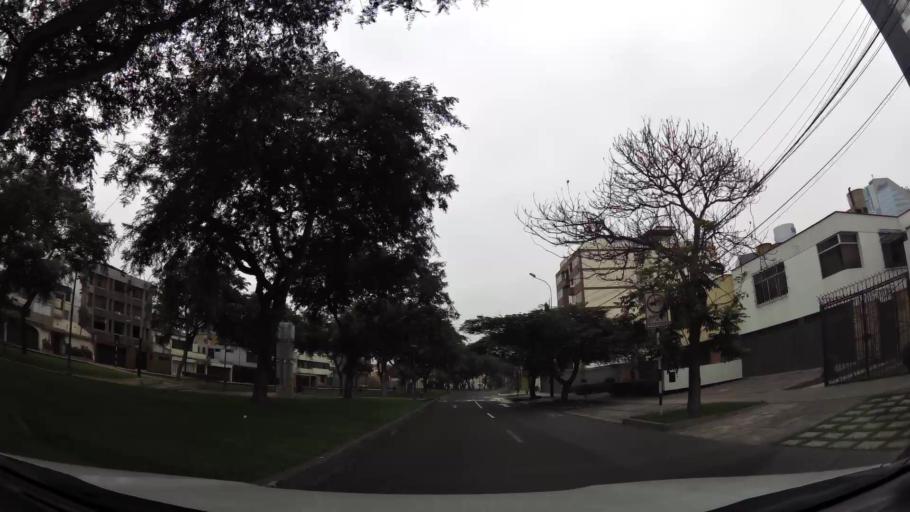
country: PE
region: Lima
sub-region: Lima
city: San Luis
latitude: -12.0954
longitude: -77.0188
